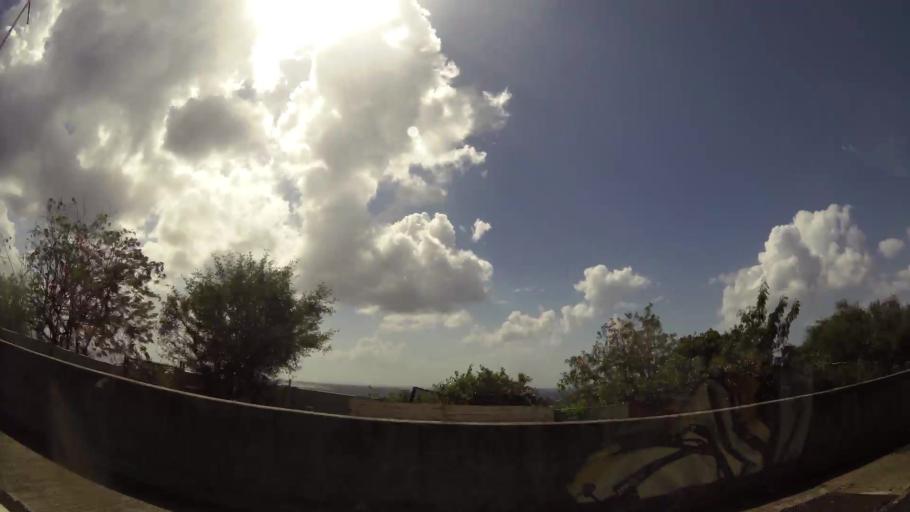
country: MQ
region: Martinique
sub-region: Martinique
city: Fort-de-France
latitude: 14.6285
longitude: -61.1182
